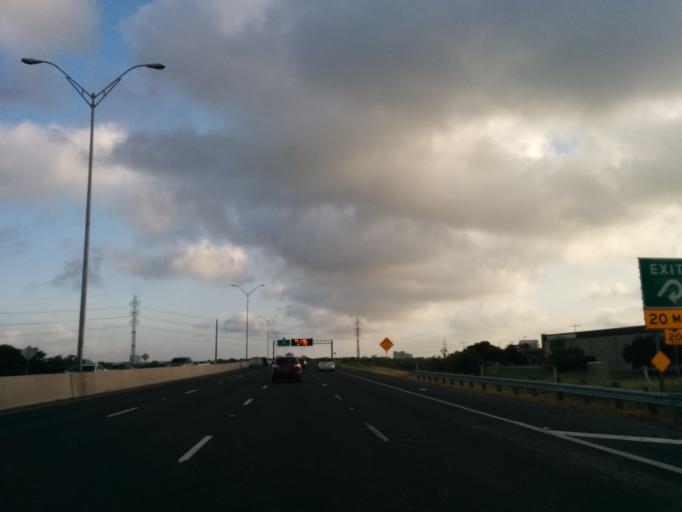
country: US
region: Texas
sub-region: Bexar County
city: Olmos Park
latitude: 29.4916
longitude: -98.4836
